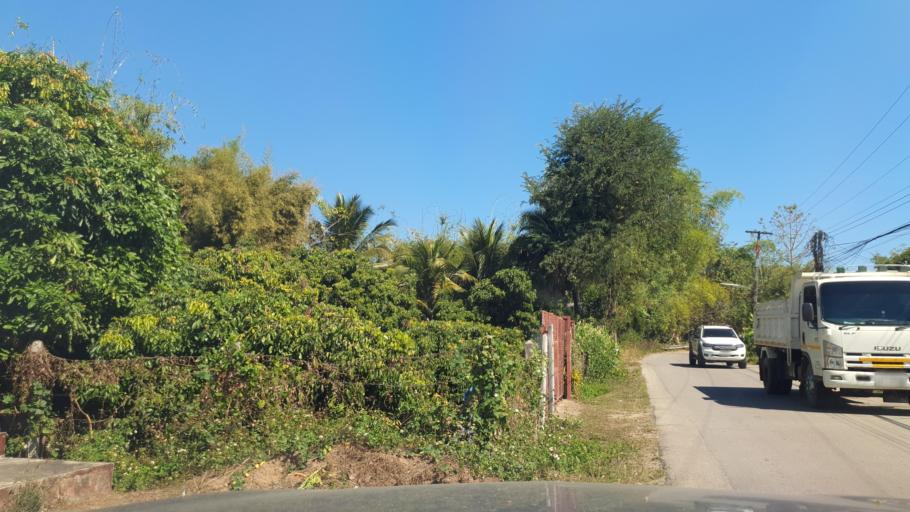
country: TH
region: Chiang Mai
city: Mae Wang
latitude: 18.6642
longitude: 98.8279
